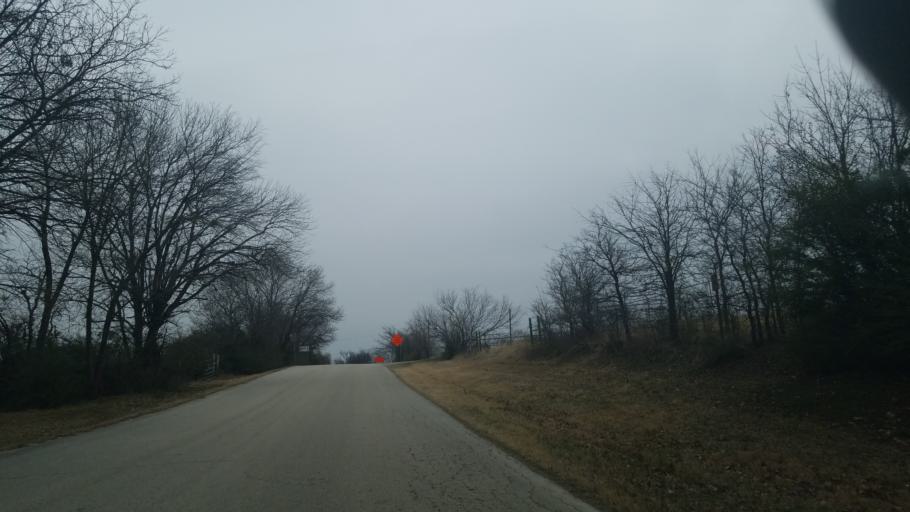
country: US
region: Texas
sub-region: Denton County
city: Argyle
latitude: 33.1471
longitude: -97.1464
